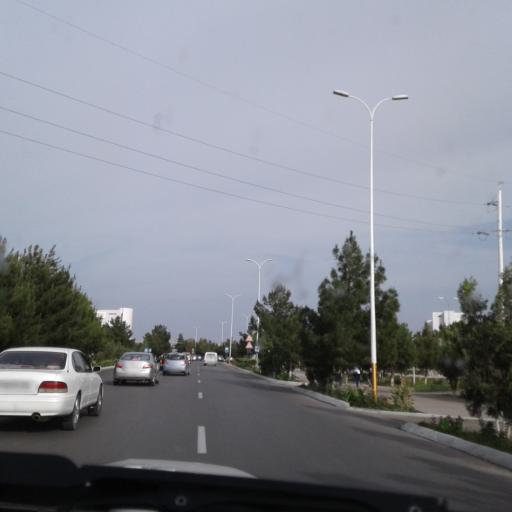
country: TM
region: Mary
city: Mary
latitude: 37.5858
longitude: 61.8561
